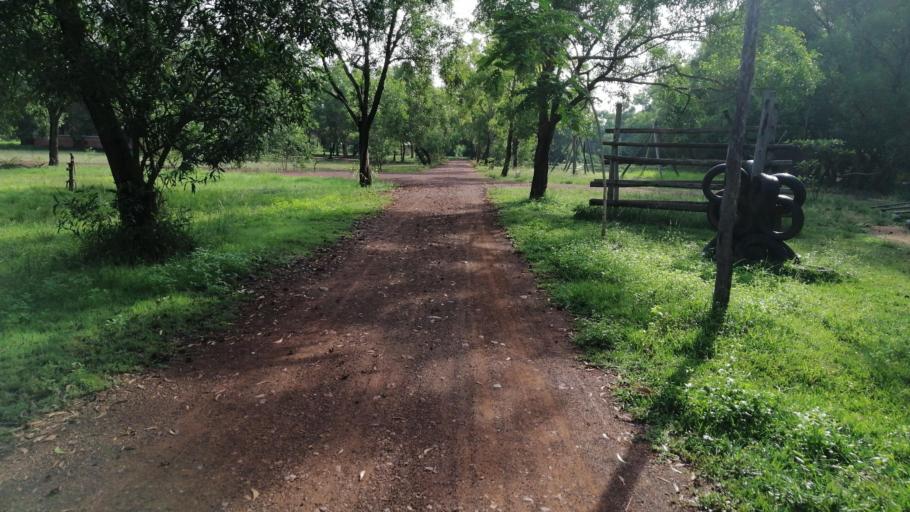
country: KH
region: Siem Reap
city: Siem Reap
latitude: 13.3511
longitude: 103.8202
